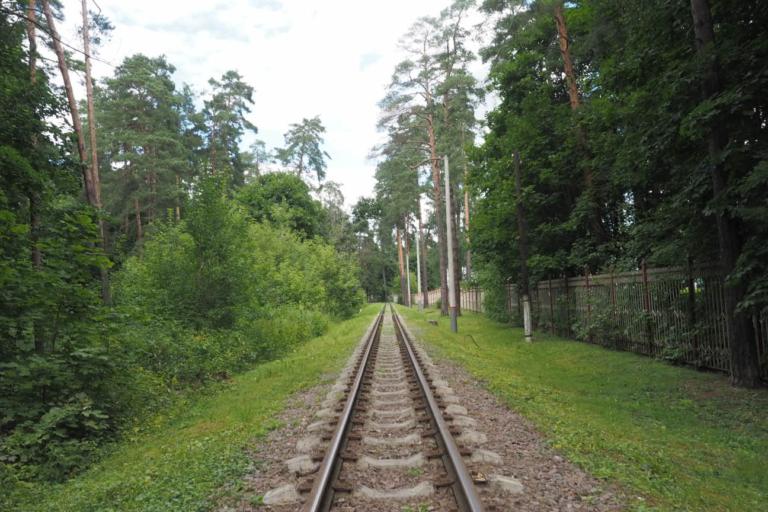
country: RU
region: Moskovskaya
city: Zhukovskiy
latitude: 55.5963
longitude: 38.1434
